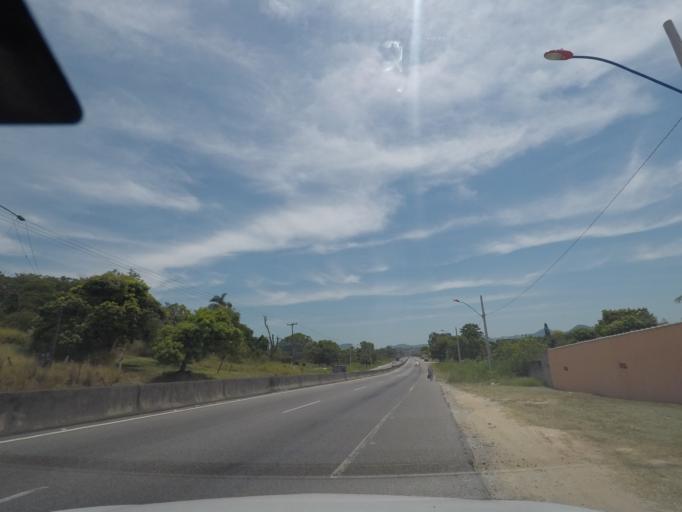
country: BR
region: Rio de Janeiro
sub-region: Marica
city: Marica
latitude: -22.9203
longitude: -42.8557
